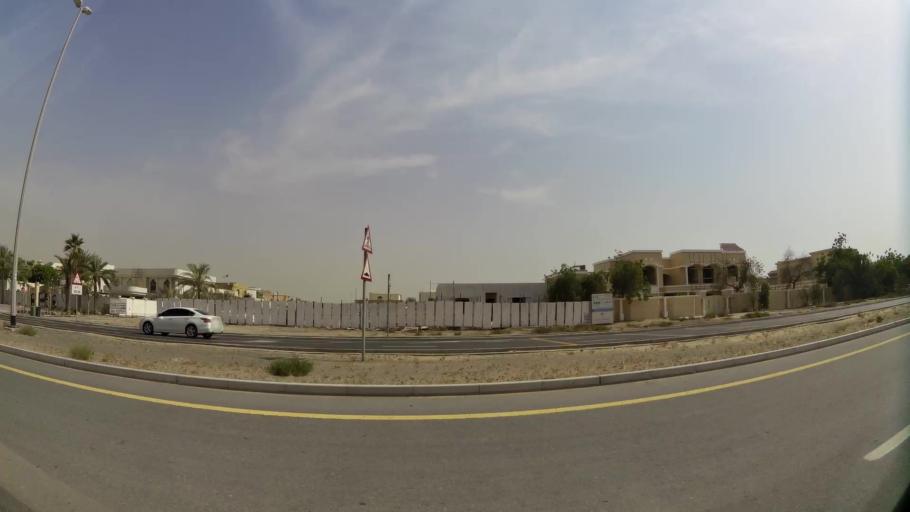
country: AE
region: Ash Shariqah
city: Sharjah
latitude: 25.2556
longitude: 55.4677
